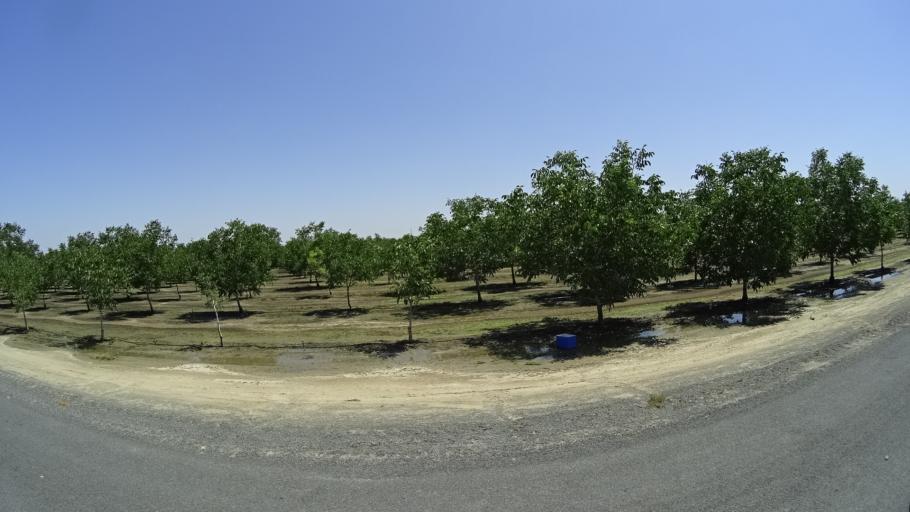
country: US
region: California
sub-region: Kings County
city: Armona
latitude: 36.2951
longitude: -119.7272
